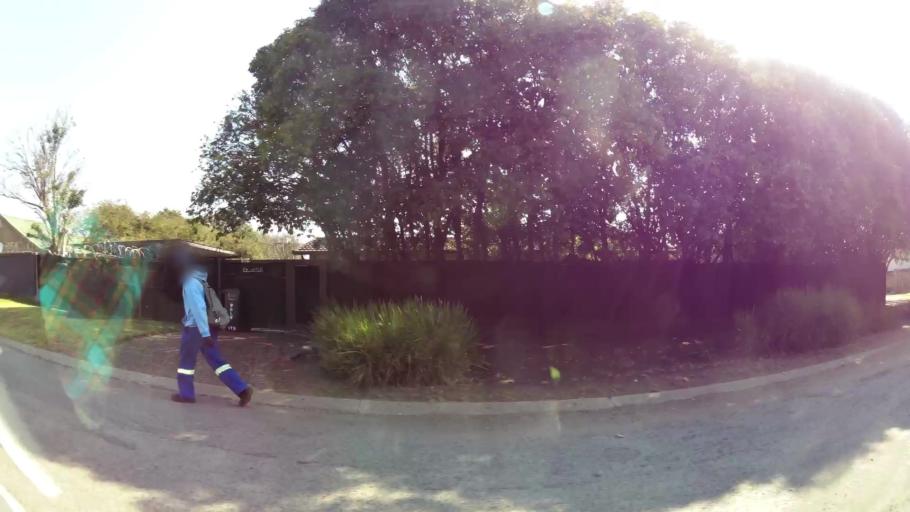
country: ZA
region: Gauteng
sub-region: City of Johannesburg Metropolitan Municipality
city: Modderfontein
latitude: -26.1216
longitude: 28.2243
